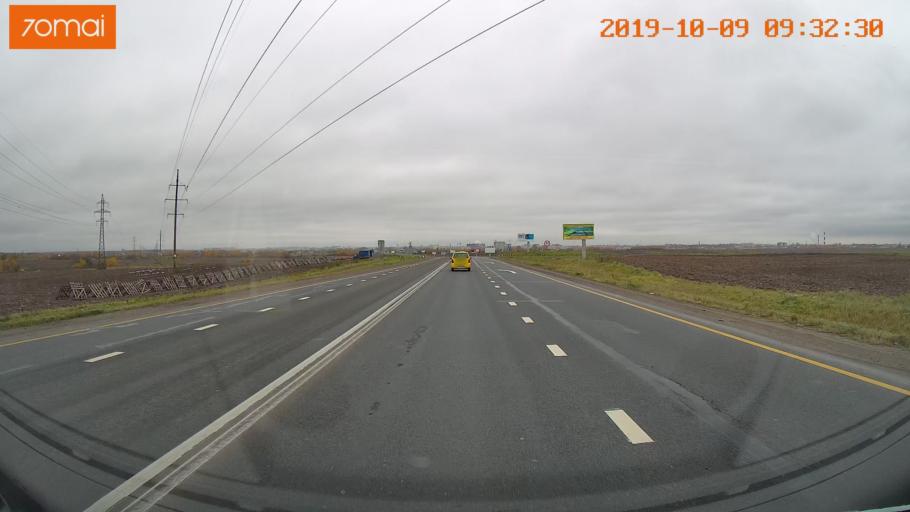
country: RU
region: Vologda
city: Vologda
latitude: 59.1592
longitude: 39.9277
